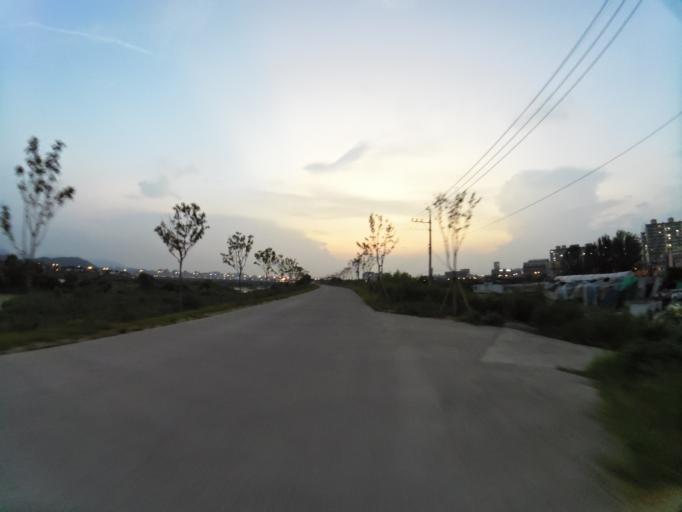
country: KR
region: Gyeongsangbuk-do
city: Gyeongsan-si
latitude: 35.8625
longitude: 128.7223
